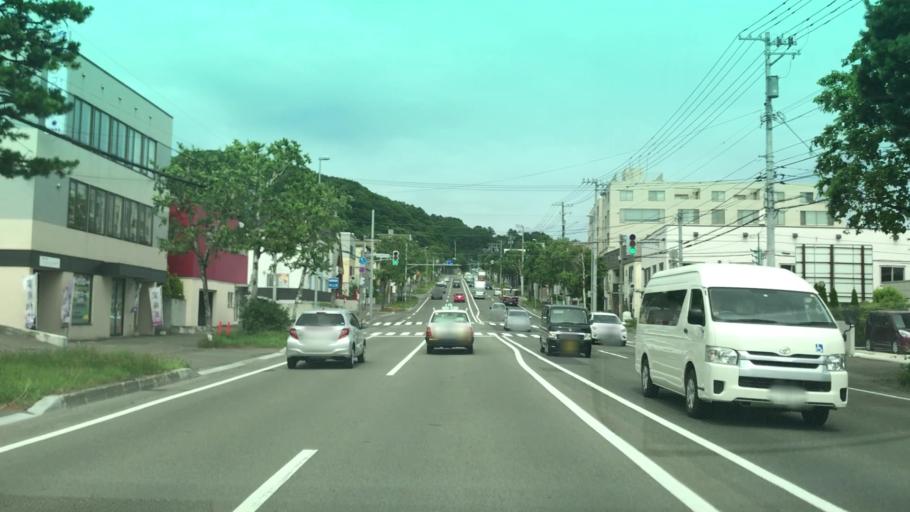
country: JP
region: Hokkaido
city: Sapporo
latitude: 43.0622
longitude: 141.2941
